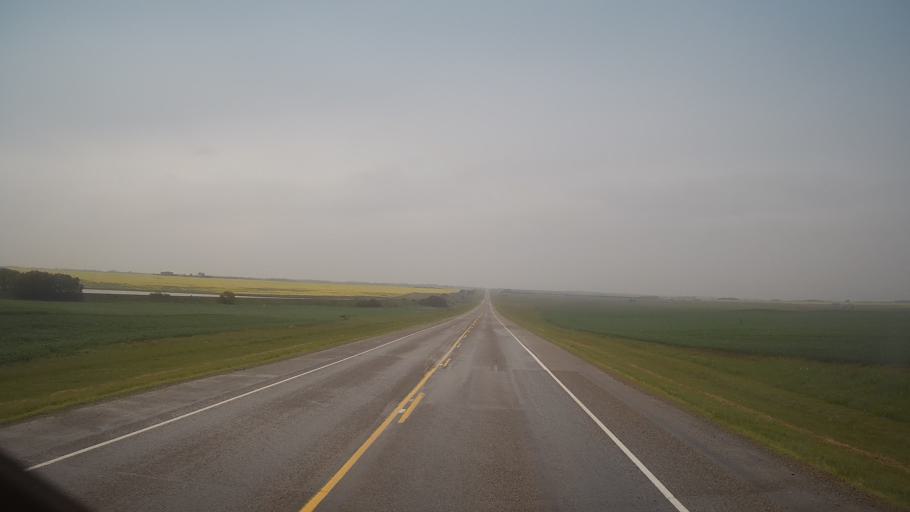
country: CA
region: Saskatchewan
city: Wilkie
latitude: 52.2097
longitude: -108.4885
